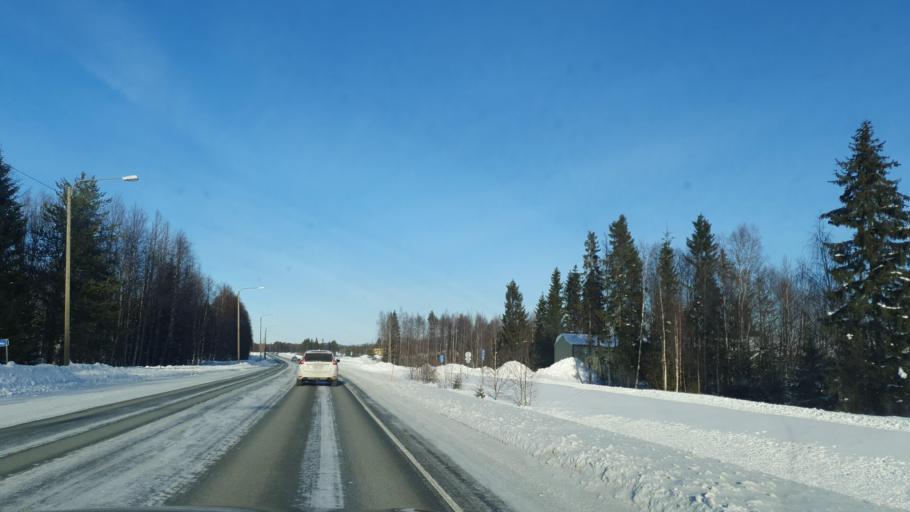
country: FI
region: Lapland
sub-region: Torniolaakso
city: Ylitornio
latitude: 66.3473
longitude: 23.6900
